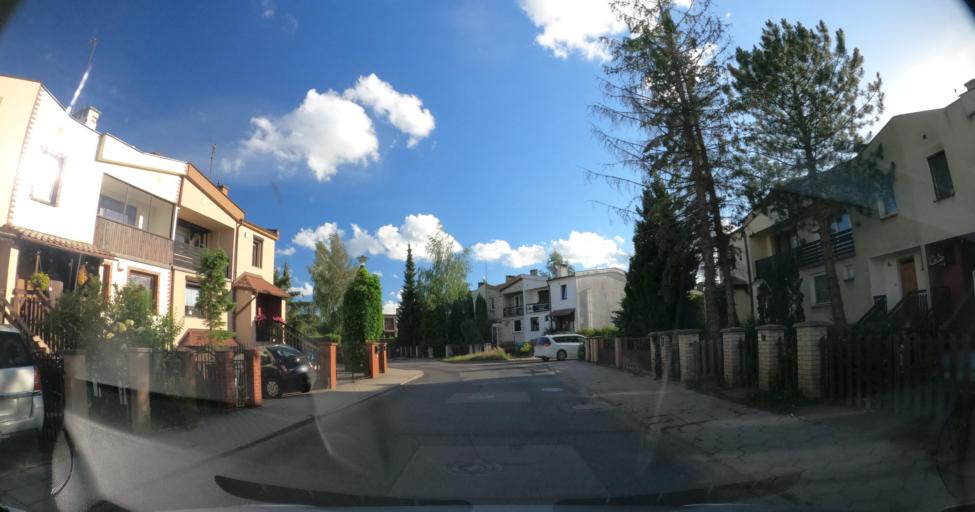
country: PL
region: Pomeranian Voivodeship
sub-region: Gdynia
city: Wielki Kack
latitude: 54.4300
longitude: 18.4745
